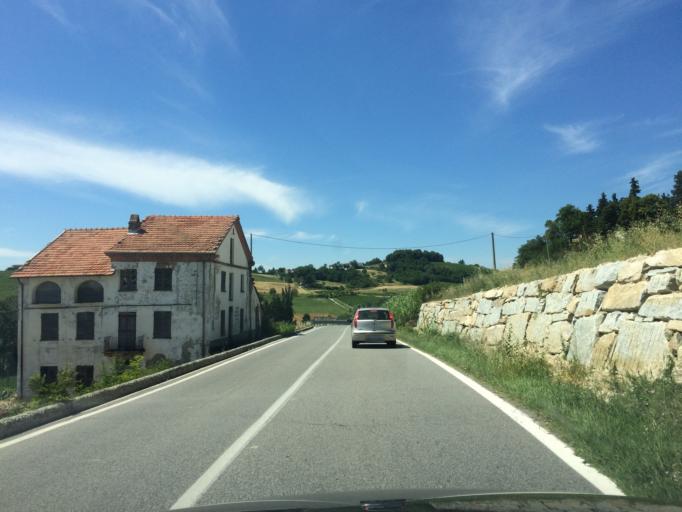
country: IT
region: Piedmont
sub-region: Provincia di Asti
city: Nizza Monferrato
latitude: 44.7522
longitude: 8.3709
